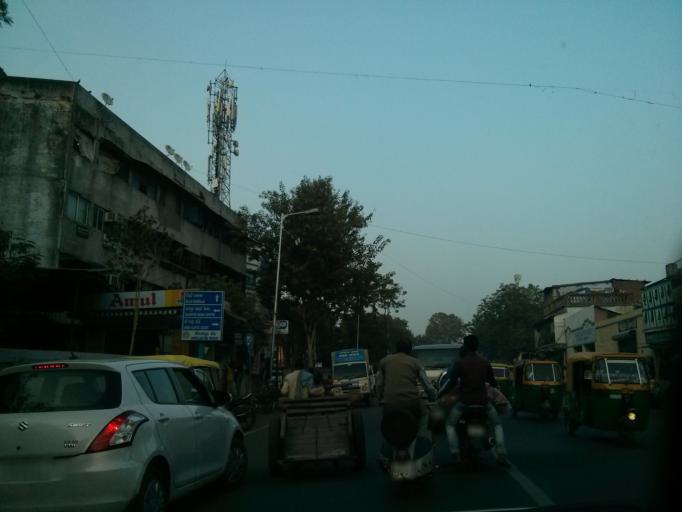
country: IN
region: Gujarat
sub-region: Ahmadabad
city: Ahmedabad
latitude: 23.0332
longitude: 72.5848
